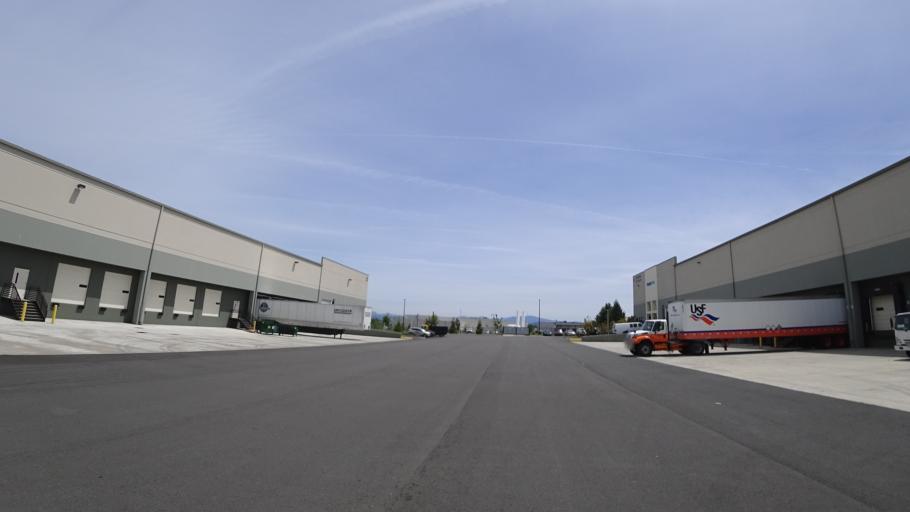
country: US
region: Oregon
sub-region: Multnomah County
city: Fairview
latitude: 45.5441
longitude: -122.4728
